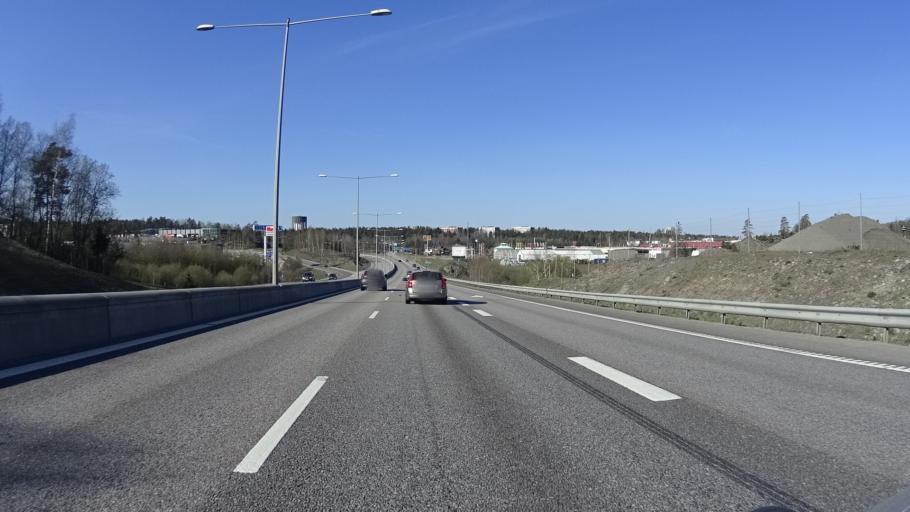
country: SE
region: Stockholm
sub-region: Sodertalje Kommun
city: Soedertaelje
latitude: 59.2028
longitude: 17.6726
